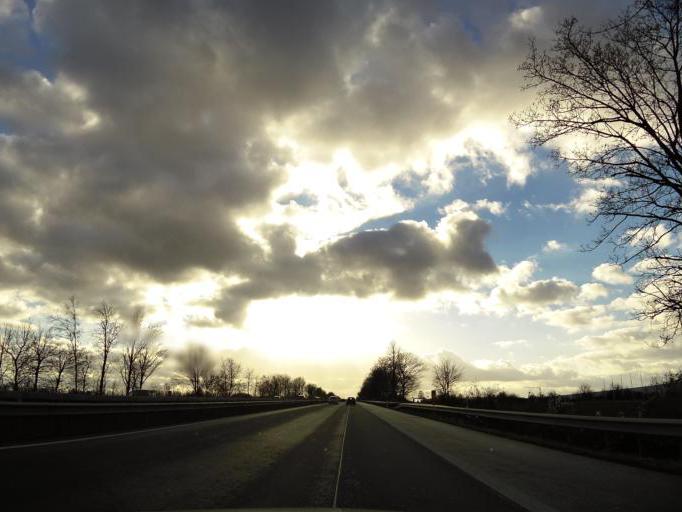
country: DE
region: Rheinland-Pfalz
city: Udenheim
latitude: 49.8798
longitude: 8.1730
